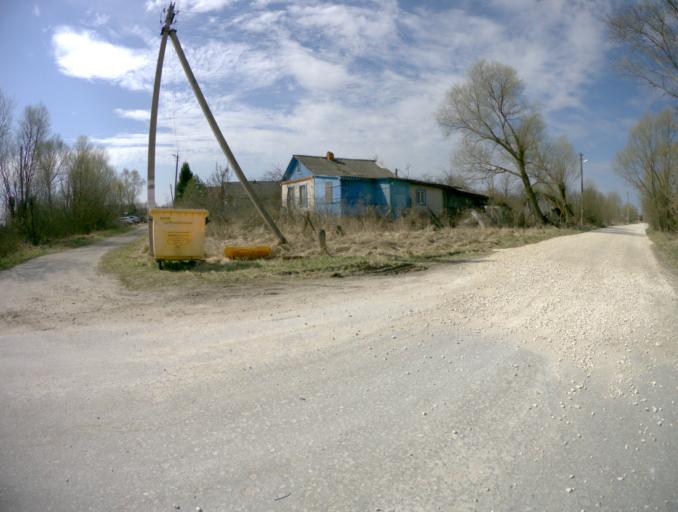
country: RU
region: Vladimir
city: Mezinovskiy
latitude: 55.4928
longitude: 40.3523
